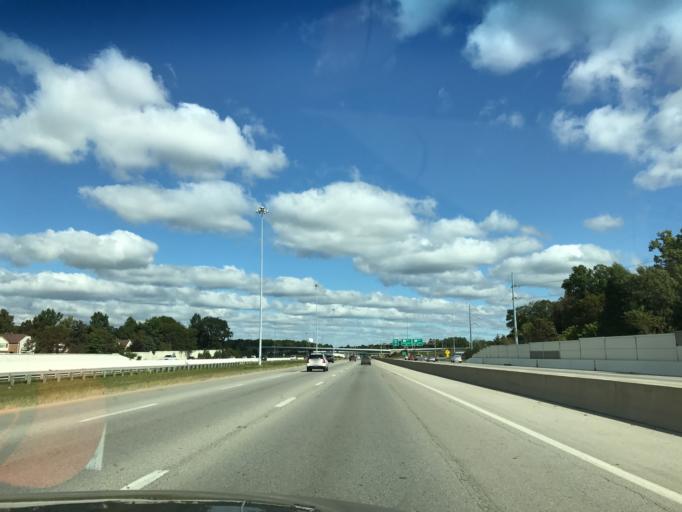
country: US
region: Ohio
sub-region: Franklin County
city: Huber Ridge
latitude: 40.0754
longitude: -82.9074
